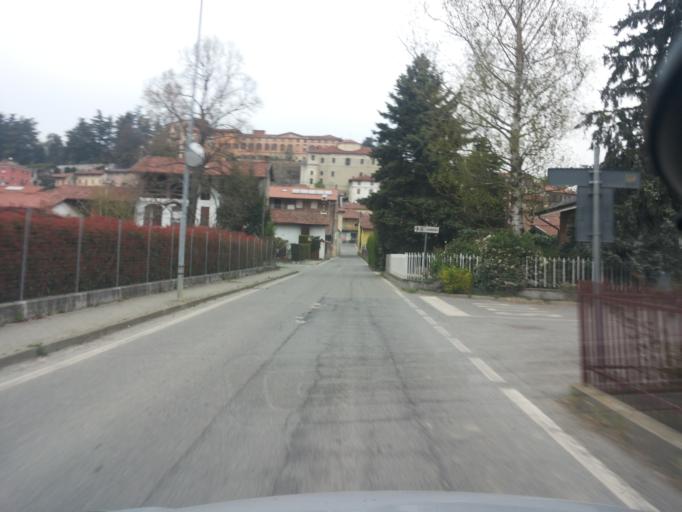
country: IT
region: Piedmont
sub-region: Provincia di Torino
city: Azeglio
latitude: 45.4226
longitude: 7.9940
